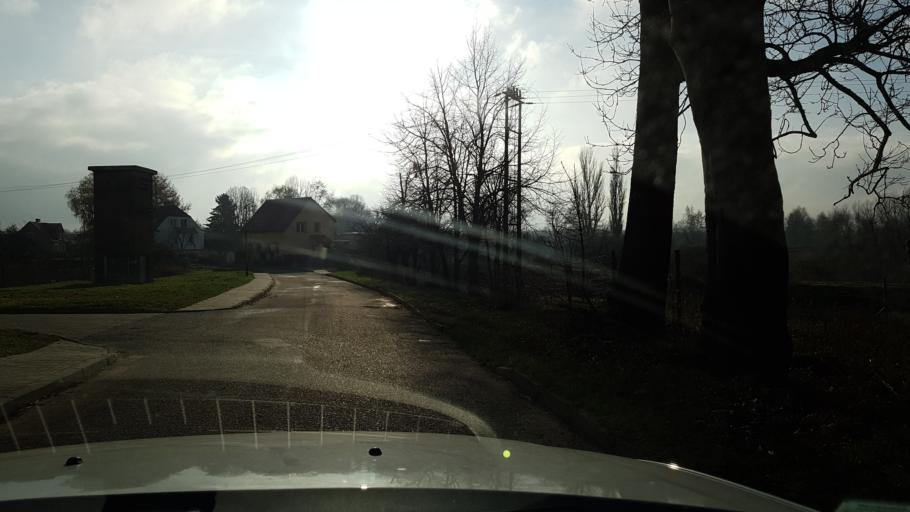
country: PL
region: West Pomeranian Voivodeship
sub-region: Powiat stargardzki
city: Insko
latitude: 53.4356
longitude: 15.5438
